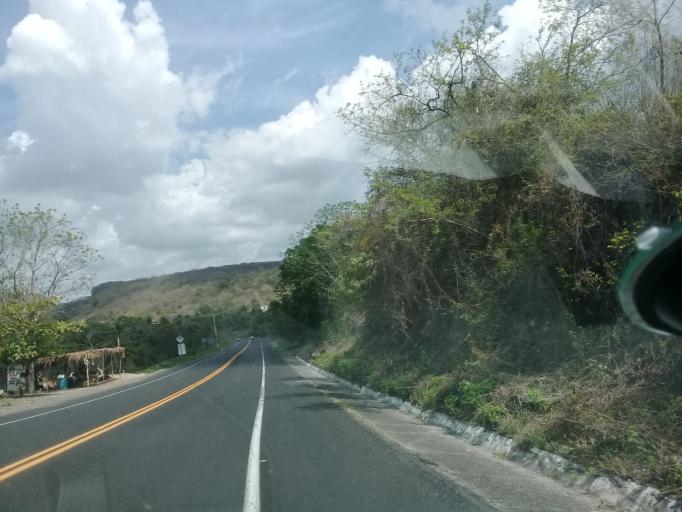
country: MX
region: Veracruz
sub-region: Emiliano Zapata
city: Plan del Rio
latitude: 19.4030
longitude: -96.6483
